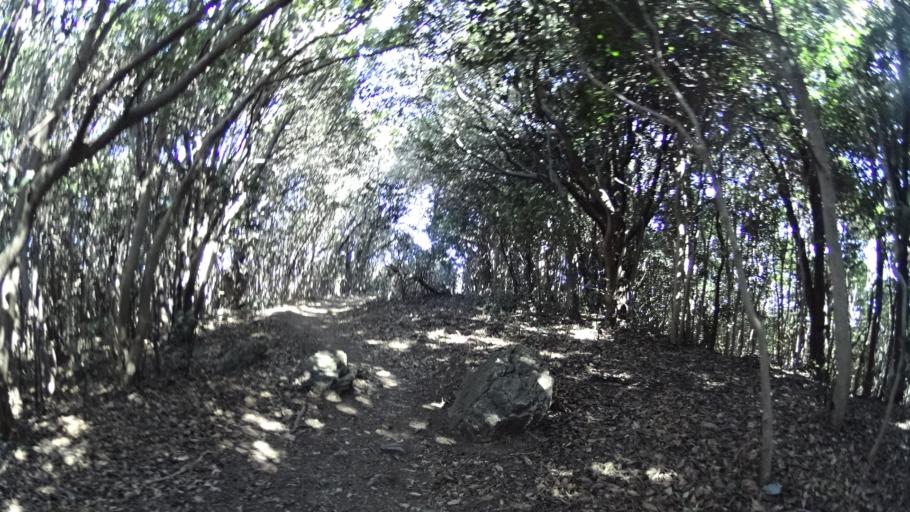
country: JP
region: Shizuoka
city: Kosai-shi
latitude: 34.7515
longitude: 137.4751
